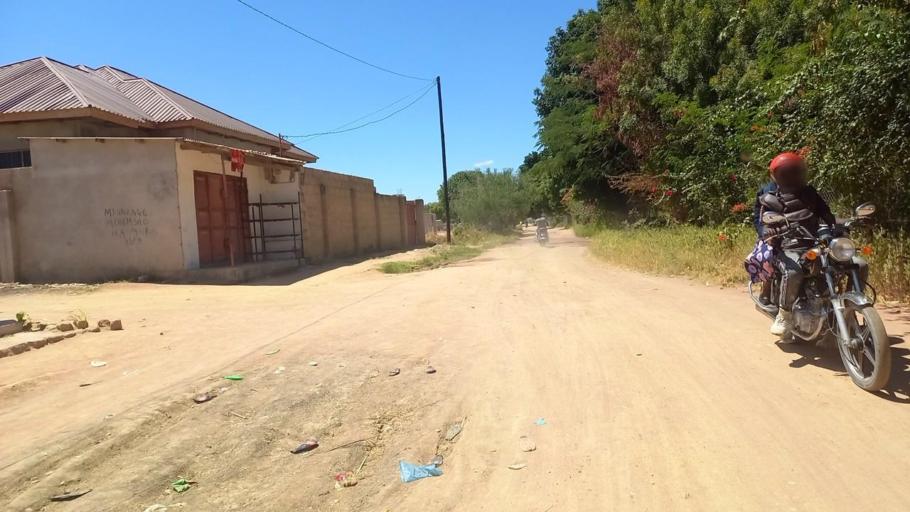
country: TZ
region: Dodoma
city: Dodoma
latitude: -6.1209
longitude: 35.7422
